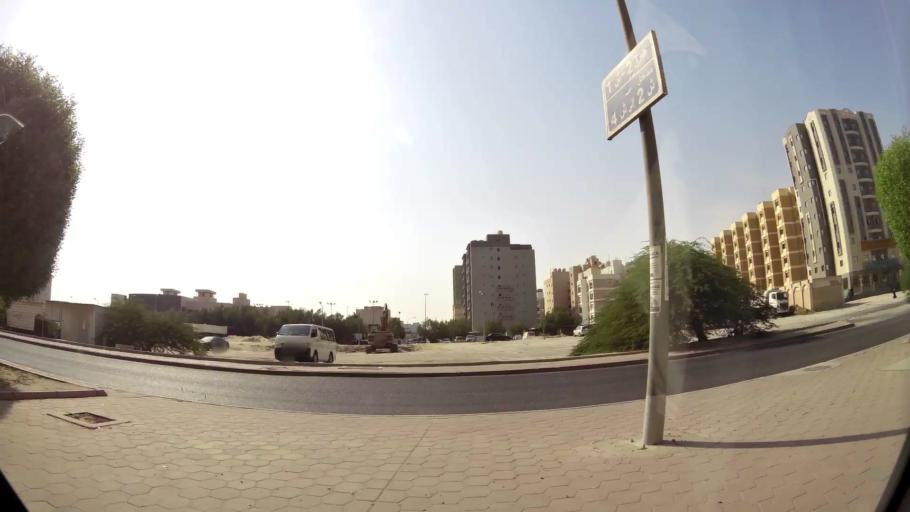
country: KW
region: Al Ahmadi
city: Al Mahbulah
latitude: 29.1363
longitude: 48.1221
